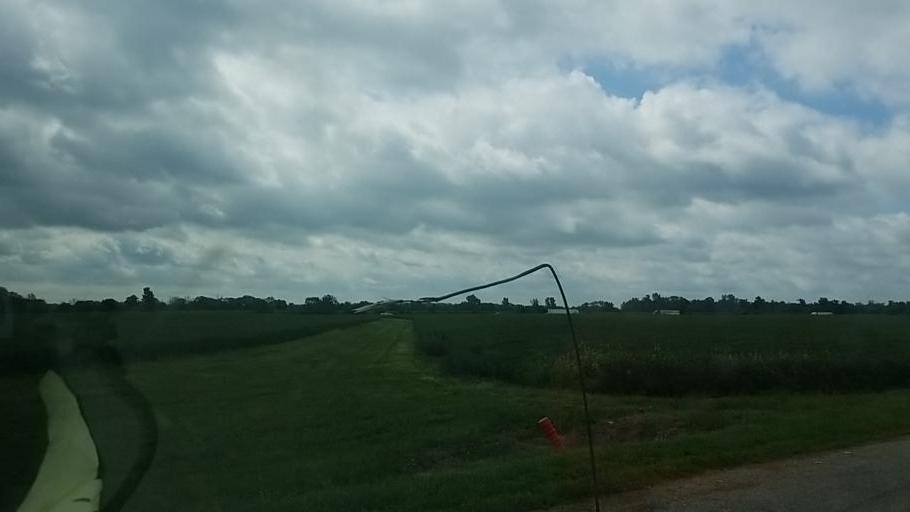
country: US
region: Ohio
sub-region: Madison County
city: Mount Sterling
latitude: 39.7907
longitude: -83.2435
